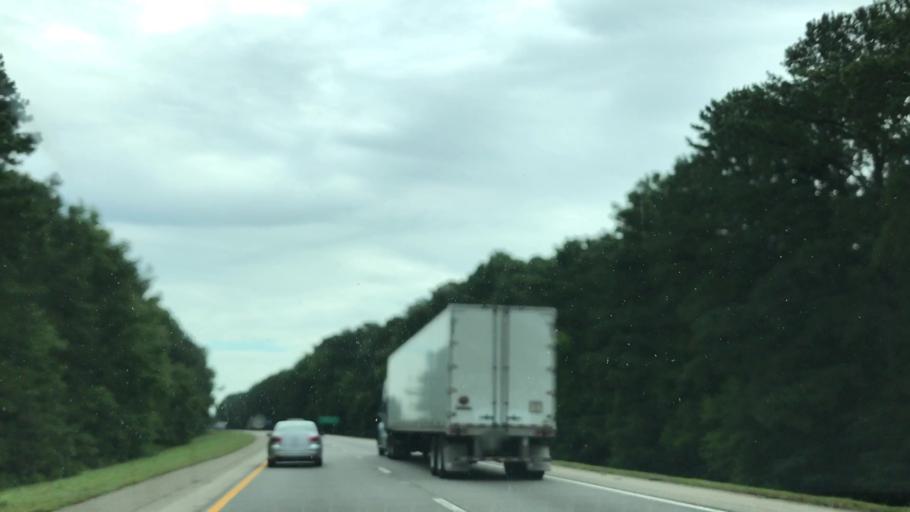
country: US
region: North Carolina
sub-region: Wilson County
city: Wilson
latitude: 35.7526
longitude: -78.0036
